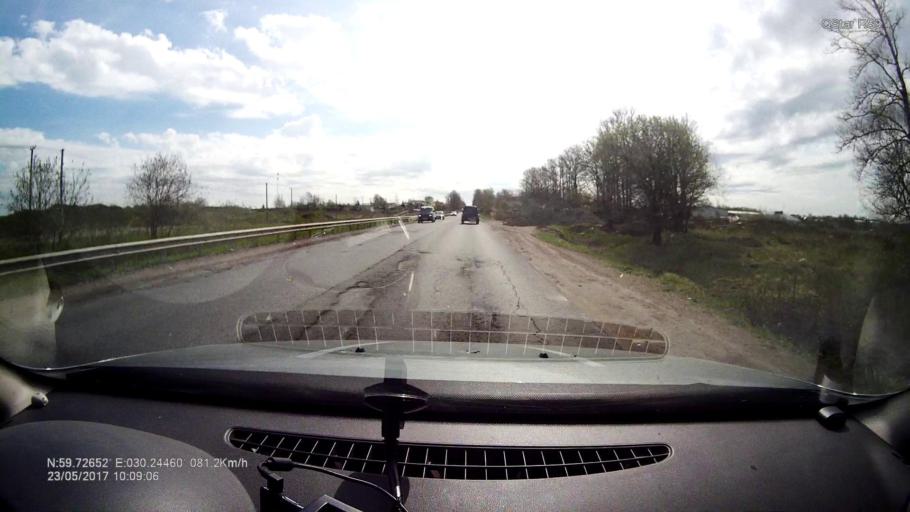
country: RU
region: St.-Petersburg
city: Aleksandrovskaya
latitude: 59.7265
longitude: 30.2445
